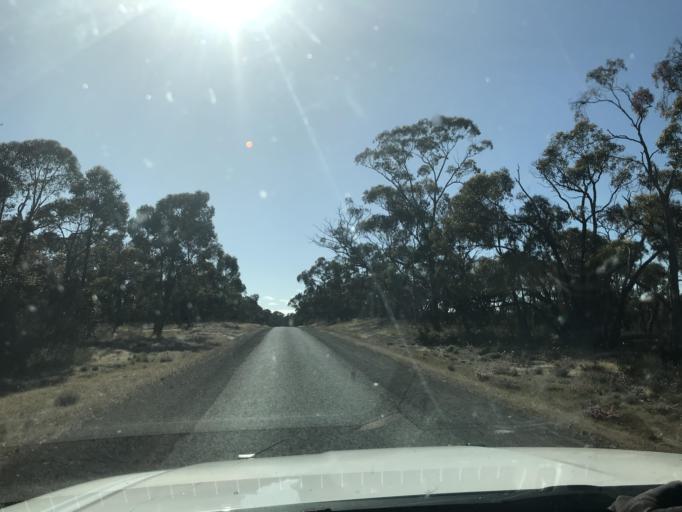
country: AU
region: Victoria
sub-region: Horsham
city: Horsham
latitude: -37.0236
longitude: 141.6898
